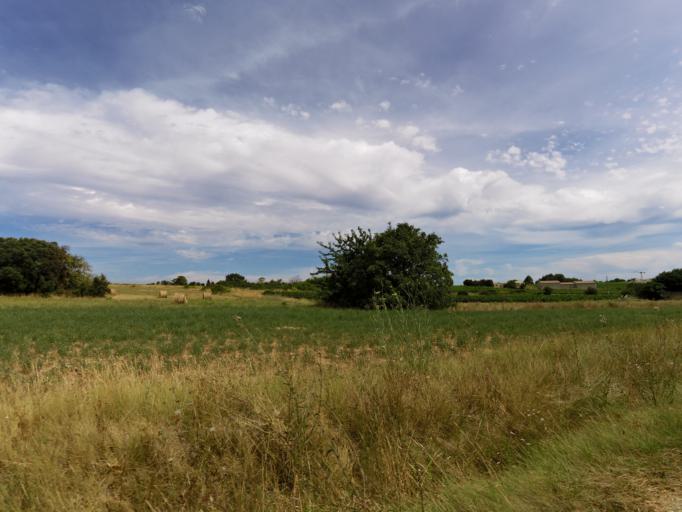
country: FR
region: Languedoc-Roussillon
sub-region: Departement du Gard
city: Saint-Mamert-du-Gard
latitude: 43.8616
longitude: 4.1604
